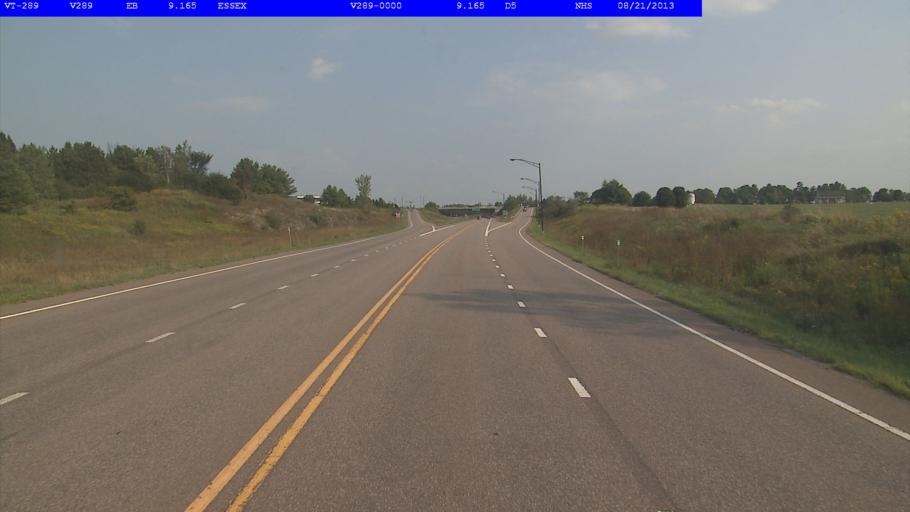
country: US
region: Vermont
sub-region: Chittenden County
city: Essex Junction
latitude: 44.5103
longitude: -73.0923
